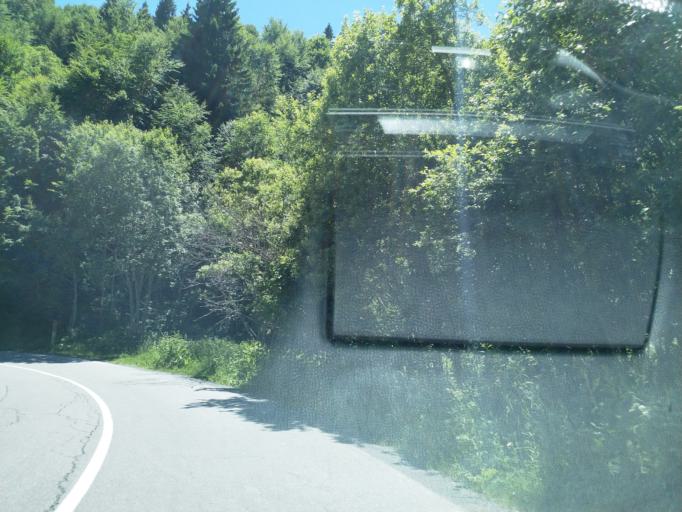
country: XK
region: Mitrovica
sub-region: Komuna e Leposaviqit
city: Leposaviq
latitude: 43.3169
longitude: 20.8437
